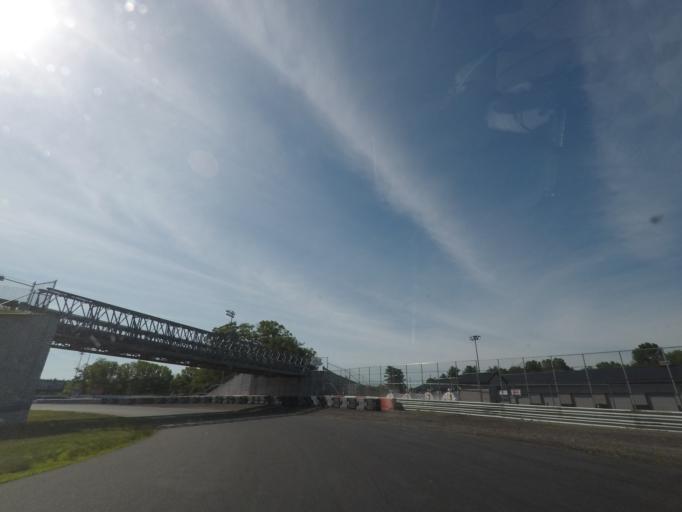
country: US
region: Connecticut
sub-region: Windham County
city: Thompson
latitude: 41.9812
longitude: -71.8269
